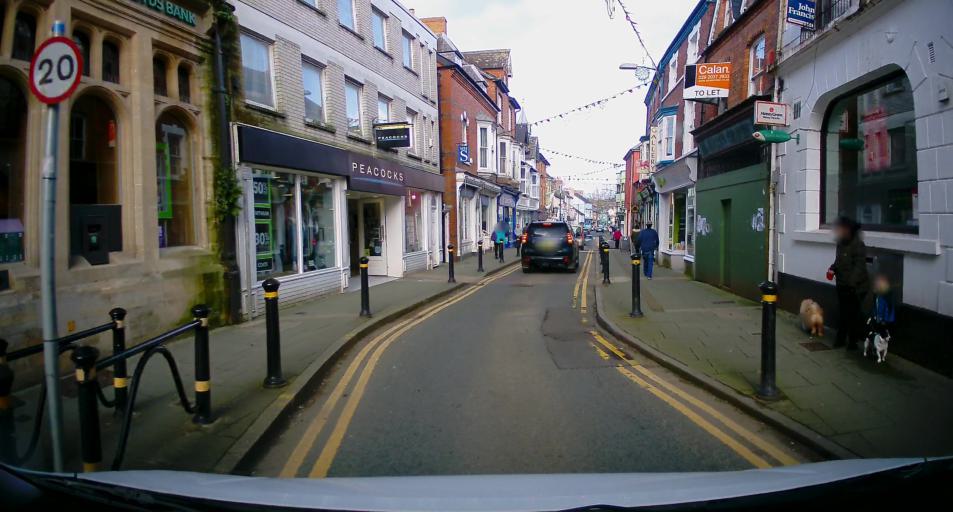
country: GB
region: Wales
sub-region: County of Ceredigion
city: Cardigan
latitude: 52.0830
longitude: -4.6612
